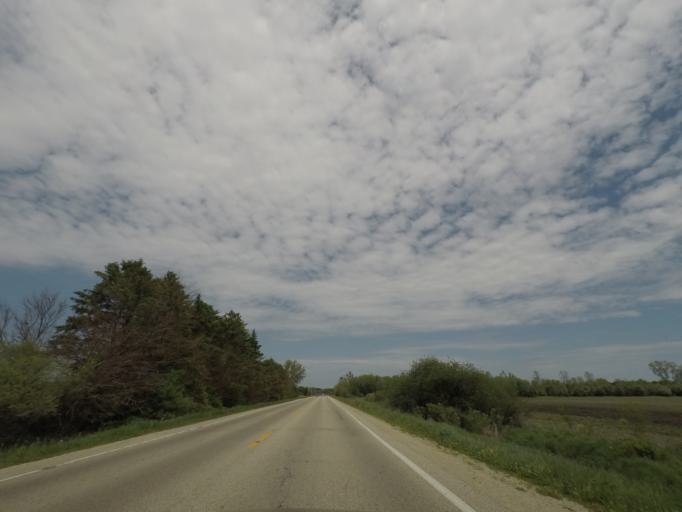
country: US
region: Wisconsin
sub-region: Rock County
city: Evansville
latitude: 42.7620
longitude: -89.2990
